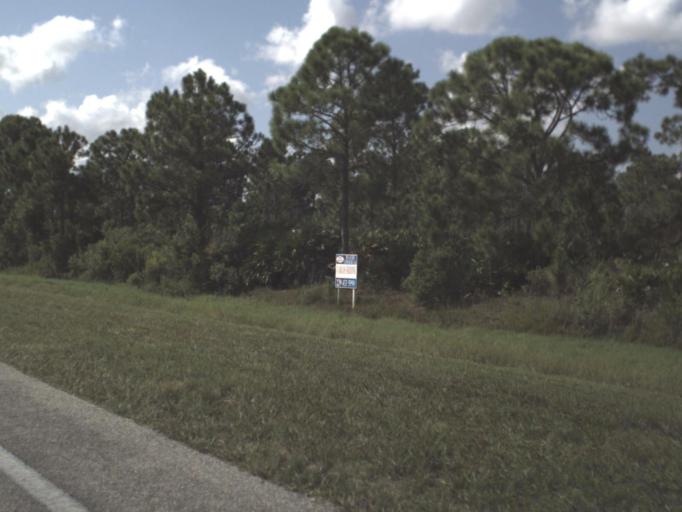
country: US
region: Florida
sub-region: Charlotte County
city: Charlotte Park
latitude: 26.8555
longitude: -81.9862
